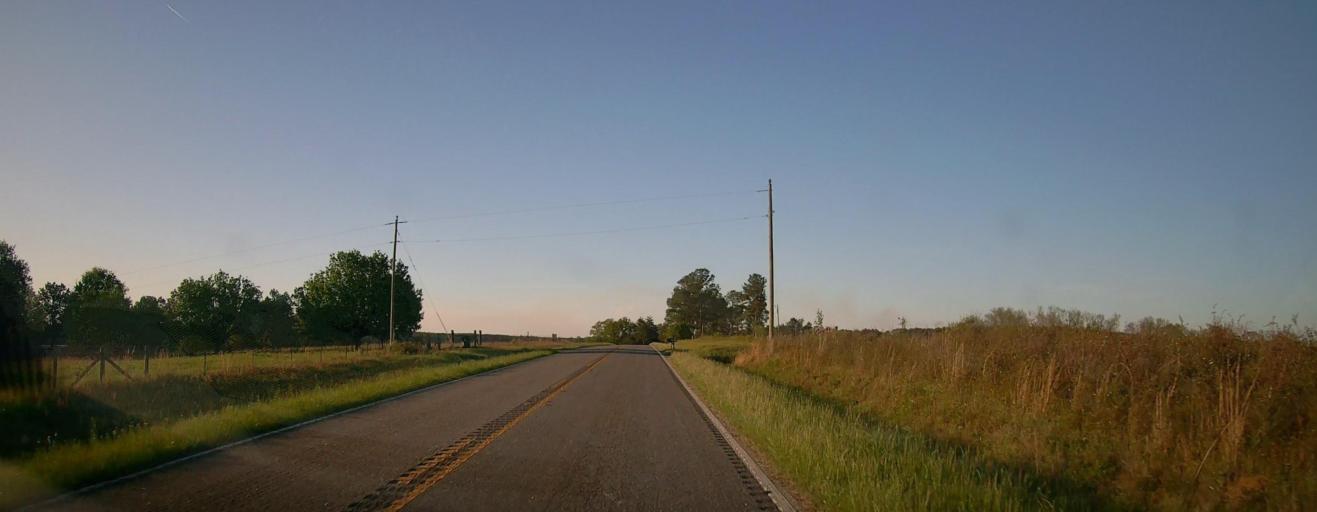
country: US
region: Georgia
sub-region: Marion County
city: Buena Vista
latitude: 32.3956
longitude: -84.4431
